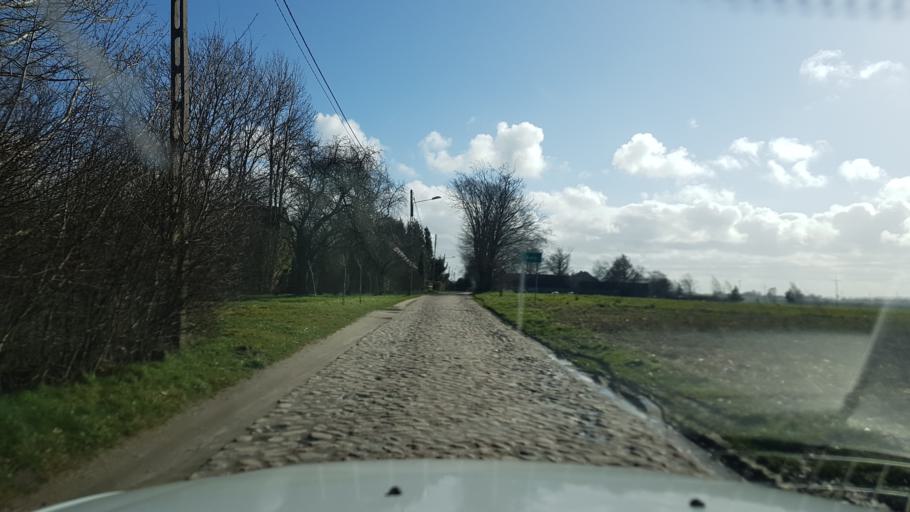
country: PL
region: West Pomeranian Voivodeship
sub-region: Powiat slawienski
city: Slawno
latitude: 54.3679
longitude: 16.5773
